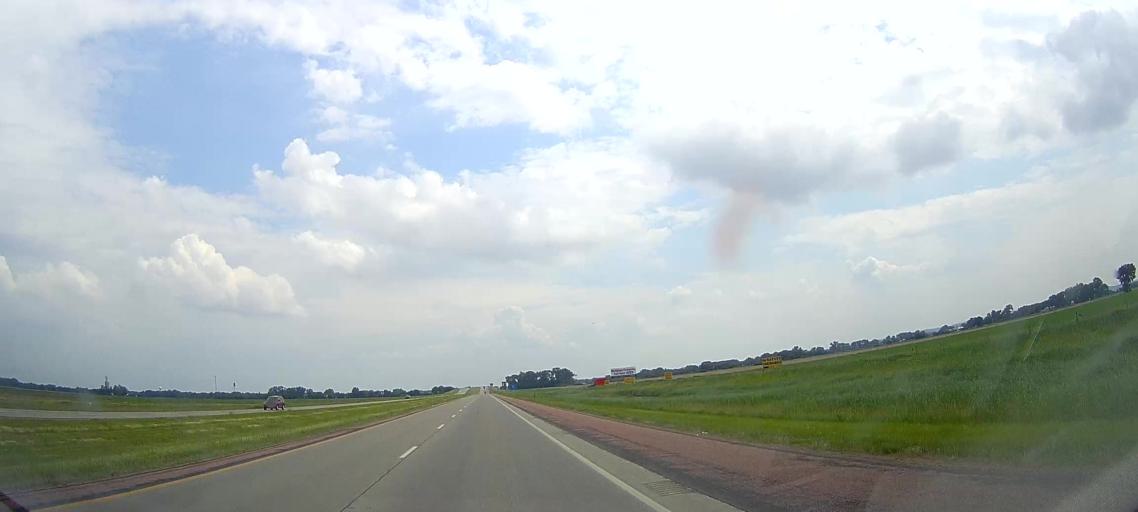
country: US
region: South Dakota
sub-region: Union County
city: Elk Point
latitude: 42.7046
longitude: -96.6974
